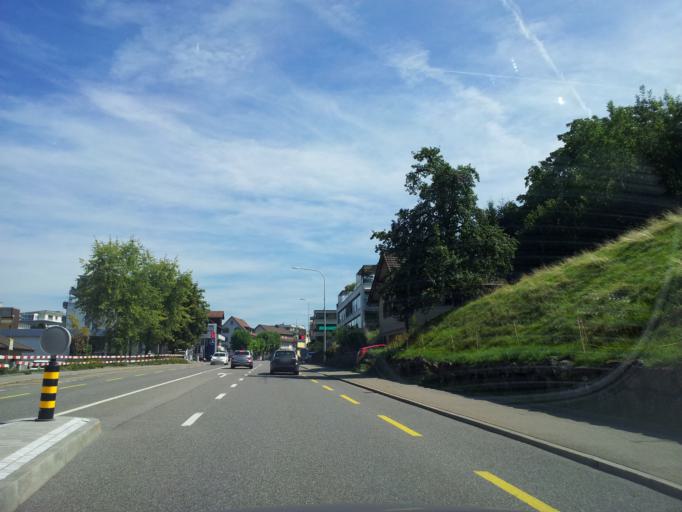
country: CH
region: Schwyz
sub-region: Bezirk March
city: Altendorf
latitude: 47.1927
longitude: 8.8272
